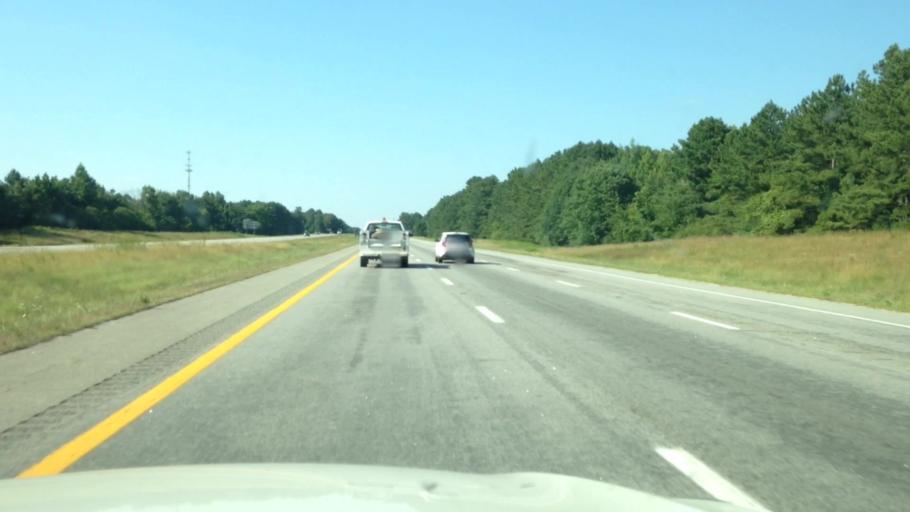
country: US
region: Virginia
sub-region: City of Emporia
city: Emporia
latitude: 36.8090
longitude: -77.4581
